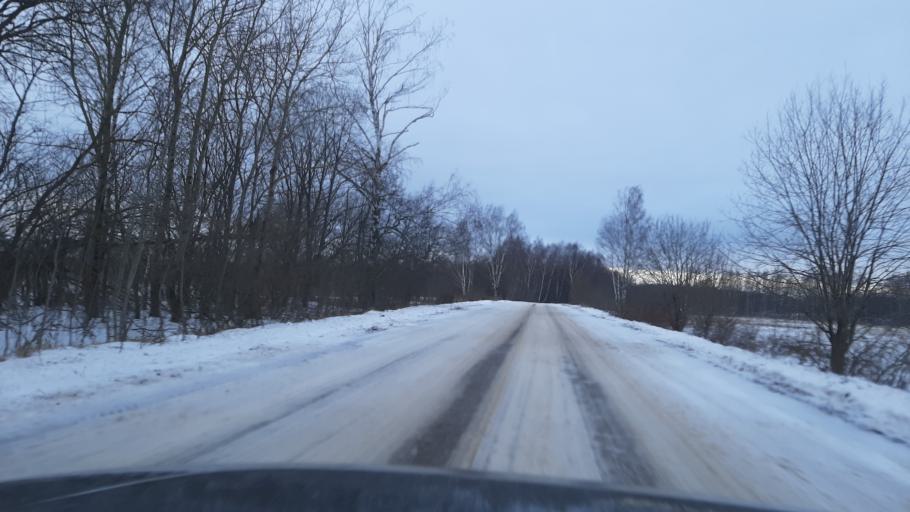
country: RU
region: Kostroma
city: Volgorechensk
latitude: 57.4377
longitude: 41.0490
